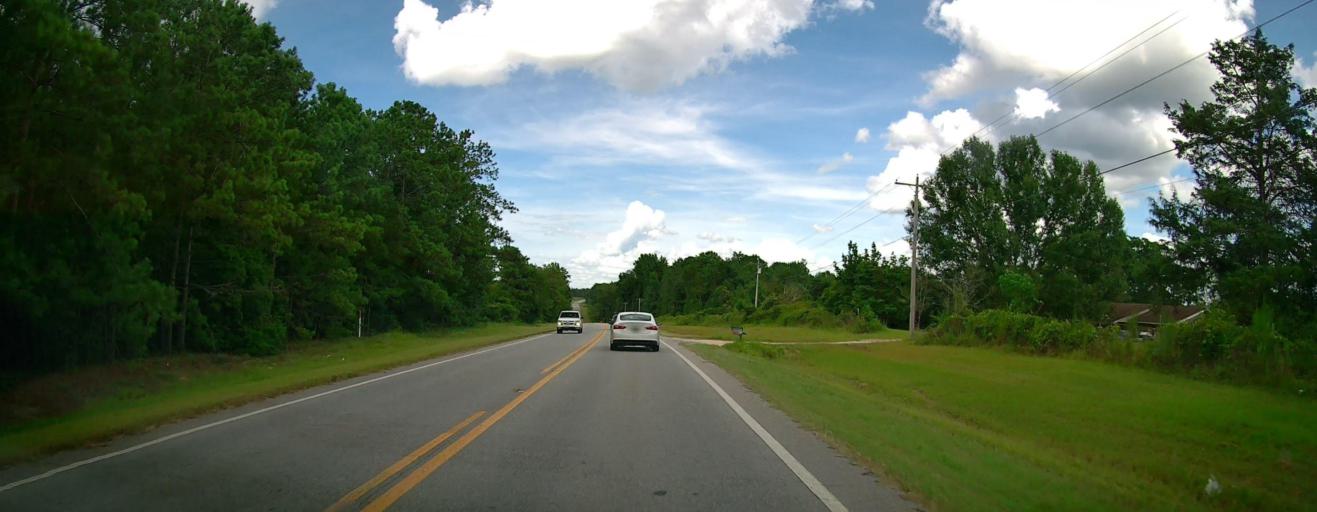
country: US
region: Alabama
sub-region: Russell County
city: Ladonia
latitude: 32.4466
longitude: -85.2452
